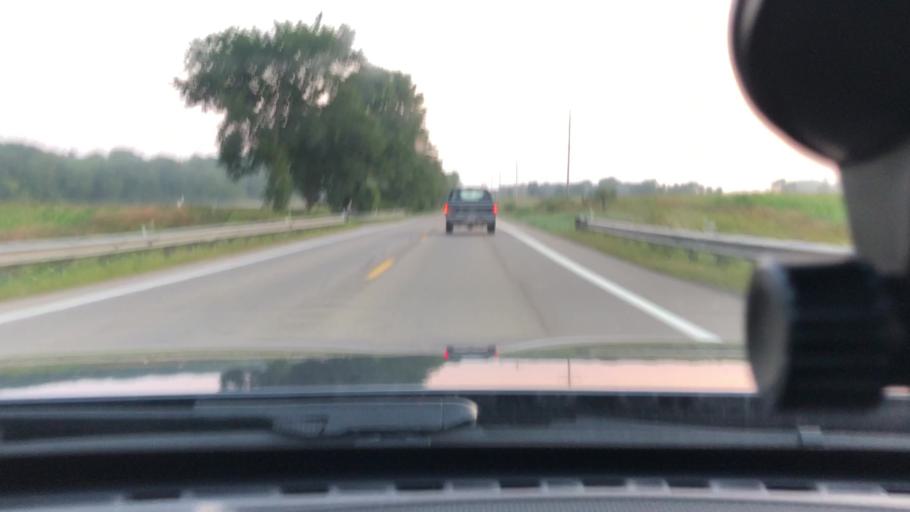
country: US
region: Michigan
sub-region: Washtenaw County
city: Chelsea
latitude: 42.2523
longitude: -84.0339
